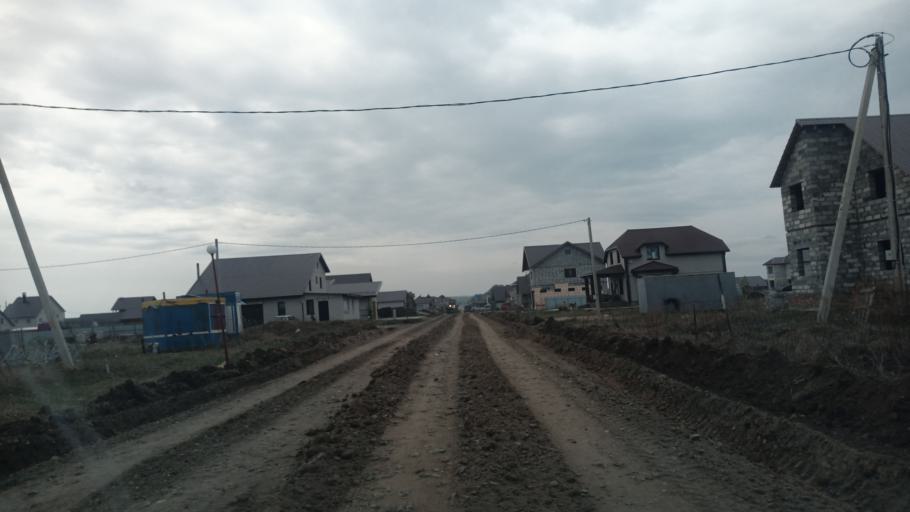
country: RU
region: Altai Krai
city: Yuzhnyy
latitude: 53.2283
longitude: 83.6913
